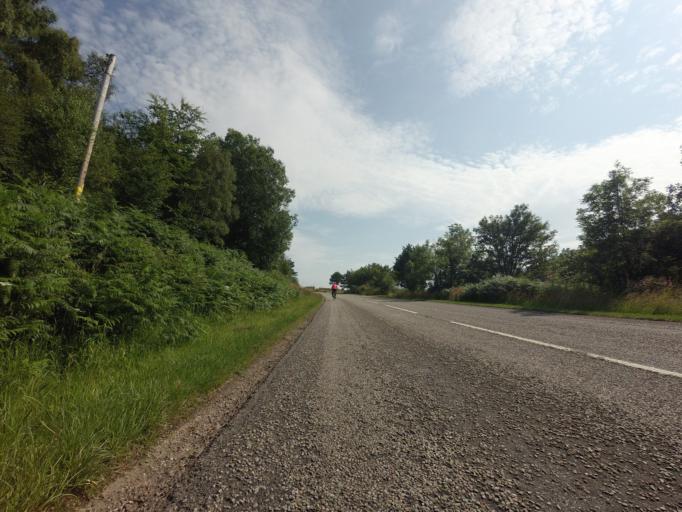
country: GB
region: Scotland
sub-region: Highland
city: Evanton
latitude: 57.9198
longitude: -4.3976
